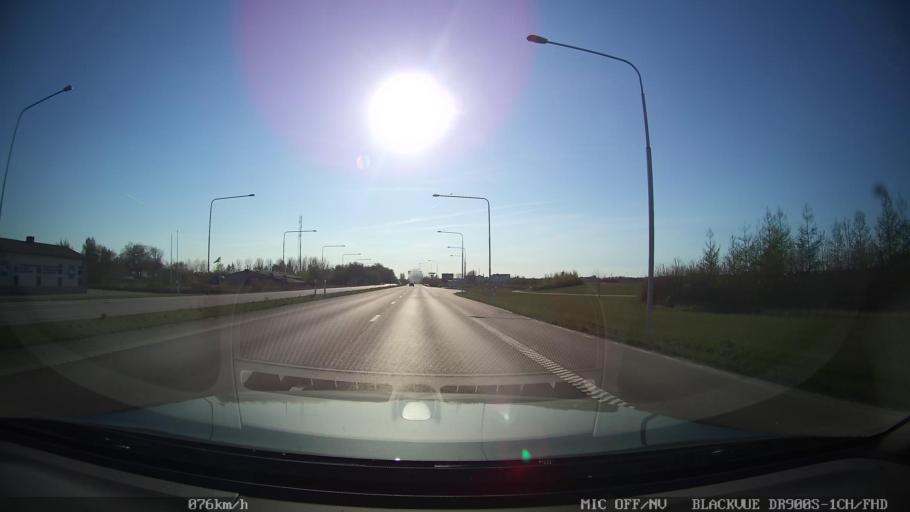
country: SE
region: Skane
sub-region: Landskrona
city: Landskrona
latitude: 55.8748
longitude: 12.8730
